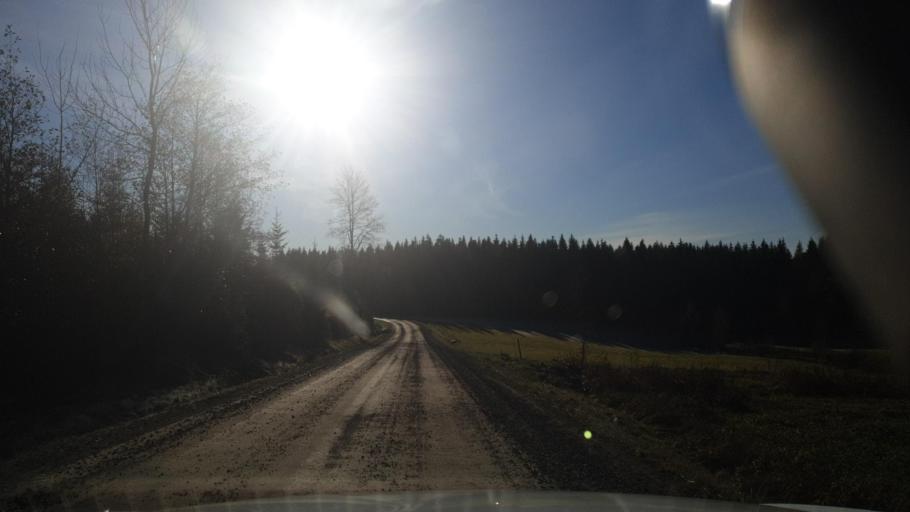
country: SE
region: Vaermland
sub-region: Karlstads Kommun
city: Edsvalla
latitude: 59.4901
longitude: 13.0320
